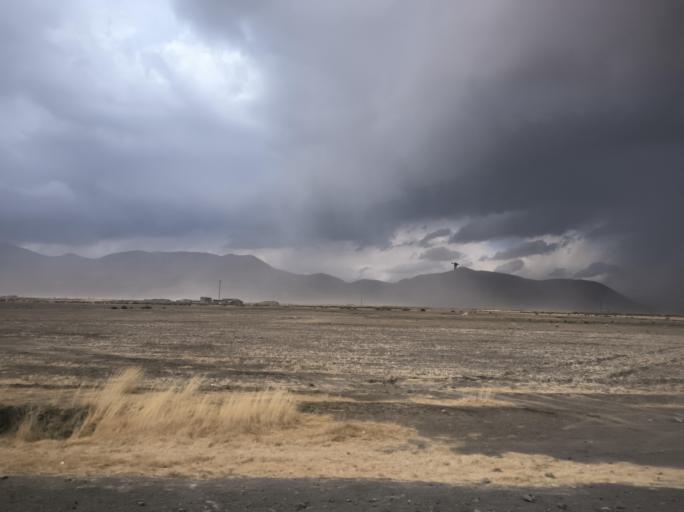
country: BO
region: Oruro
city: Challapata
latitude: -18.7794
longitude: -66.8514
